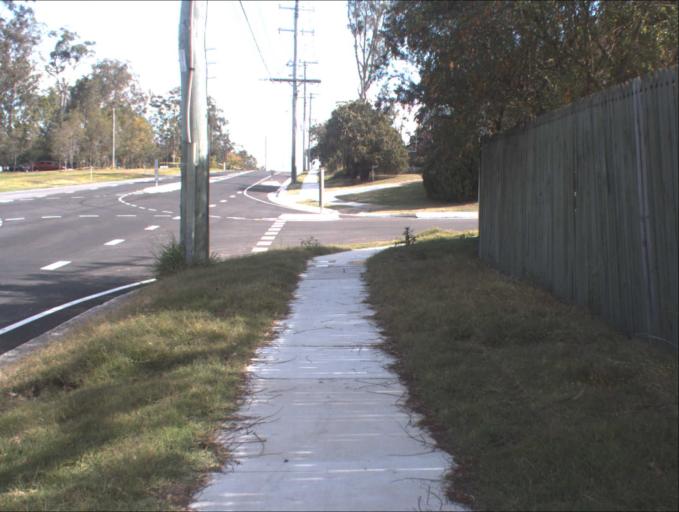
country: AU
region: Queensland
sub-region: Logan
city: Slacks Creek
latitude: -27.6484
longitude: 153.1358
